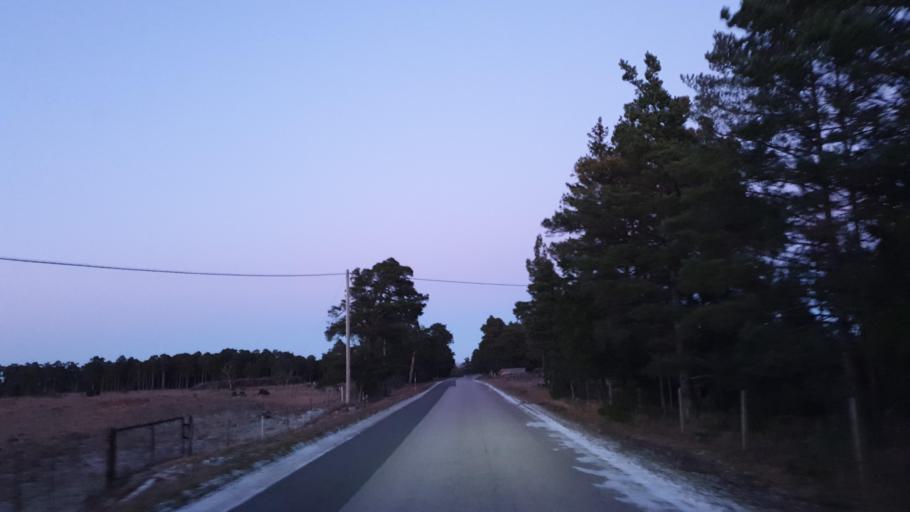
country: SE
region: Gotland
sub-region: Gotland
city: Slite
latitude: 57.4132
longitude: 18.8116
